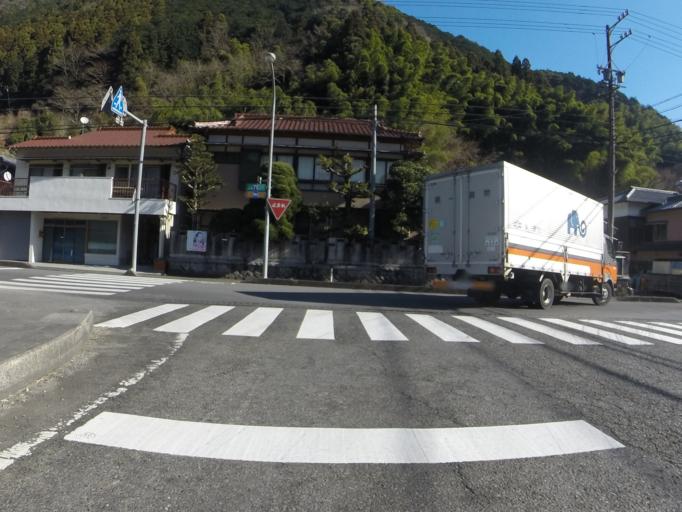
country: JP
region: Shizuoka
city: Fujinomiya
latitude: 35.1088
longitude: 138.4896
